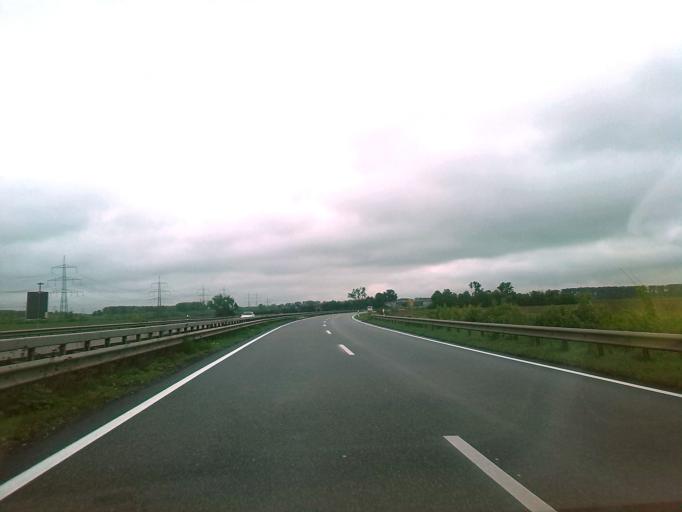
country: DE
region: Rheinland-Pfalz
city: Bobenheim-Roxheim
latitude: 49.5740
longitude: 8.3985
